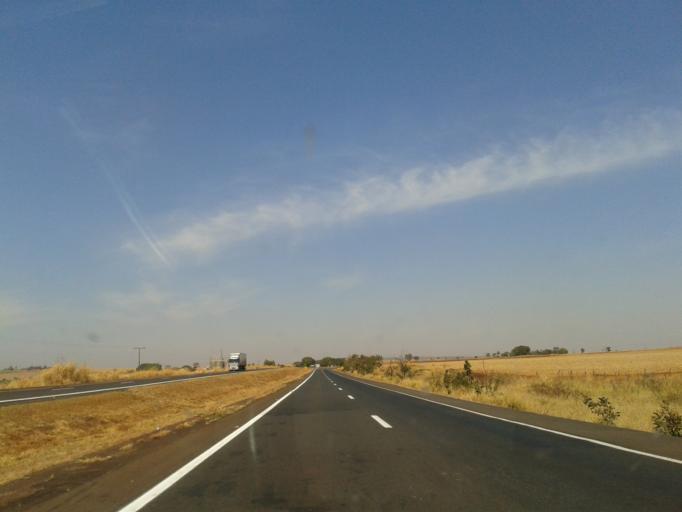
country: BR
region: Goias
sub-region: Goiatuba
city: Goiatuba
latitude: -18.1732
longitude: -49.2899
